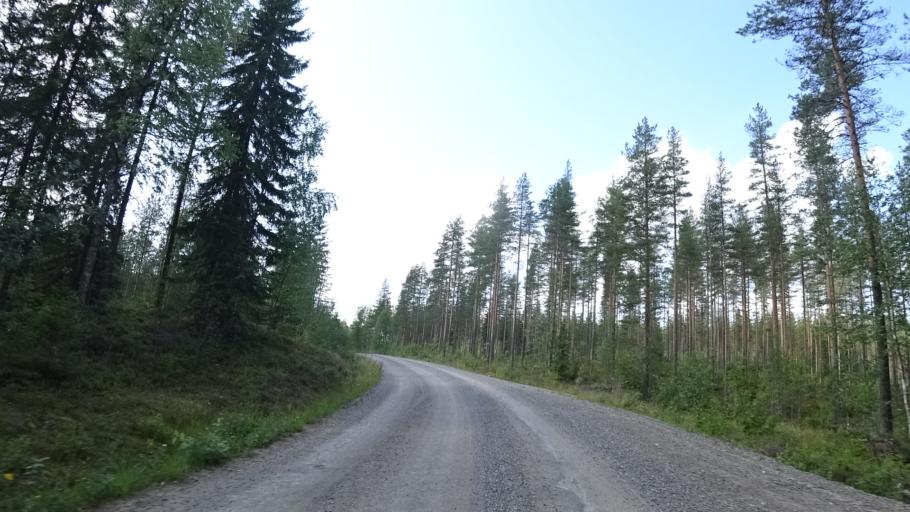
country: FI
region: North Karelia
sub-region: Joensuu
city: Ilomantsi
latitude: 62.9295
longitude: 31.3223
